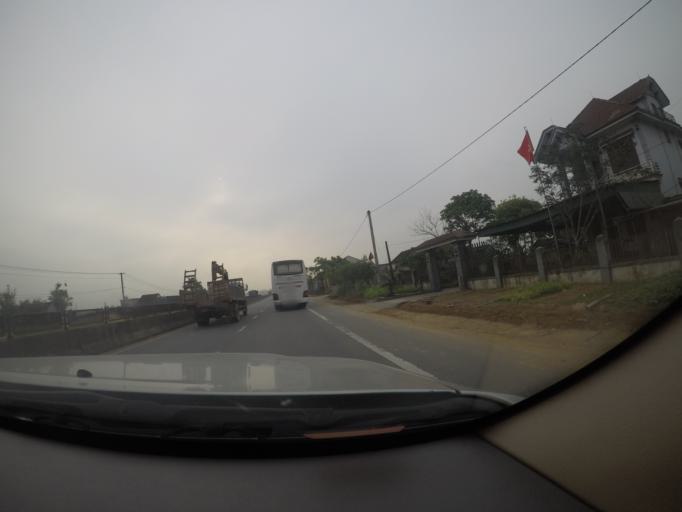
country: VN
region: Ha Tinh
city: Cam Xuyen
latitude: 18.2135
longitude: 106.1029
